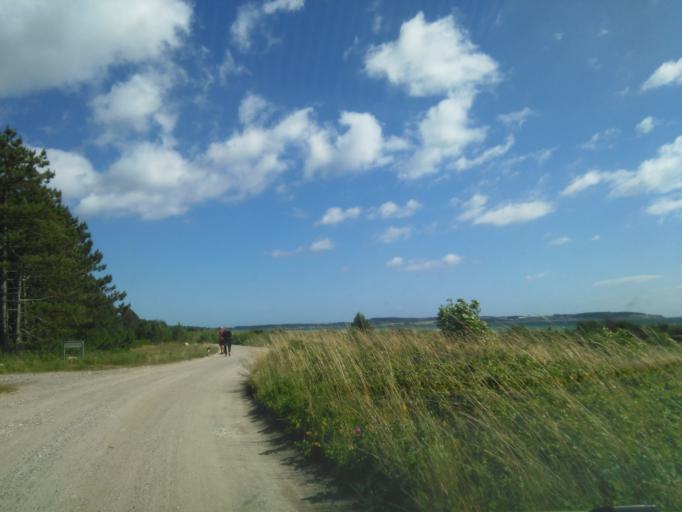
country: DK
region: Central Jutland
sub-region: Syddjurs Kommune
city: Ronde
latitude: 56.1794
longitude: 10.4748
